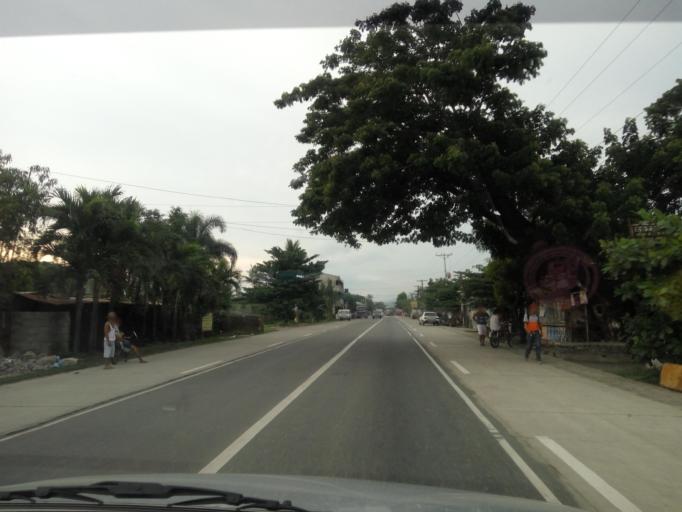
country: PH
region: Ilocos
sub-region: Province of Pangasinan
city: Bataquil
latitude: 16.1547
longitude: 120.5224
